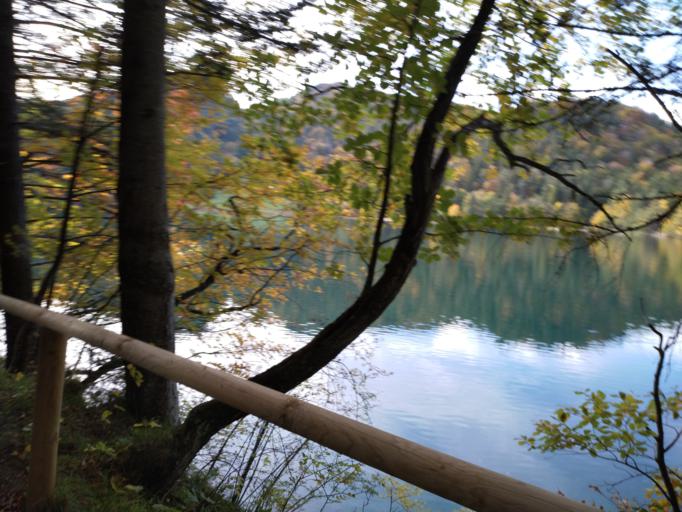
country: AT
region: Tyrol
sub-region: Politischer Bezirk Reutte
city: Vils
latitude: 47.5605
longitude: 10.6426
